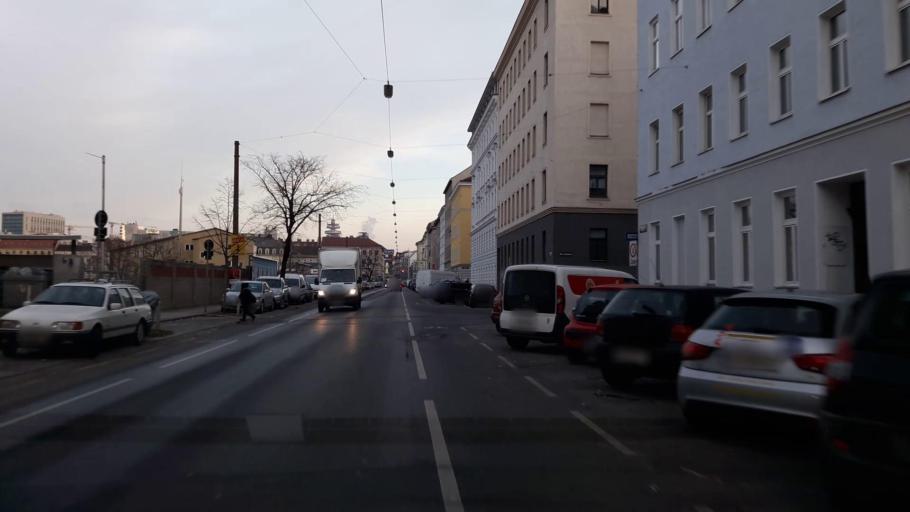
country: AT
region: Vienna
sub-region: Wien Stadt
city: Vienna
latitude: 48.1815
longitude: 16.3698
